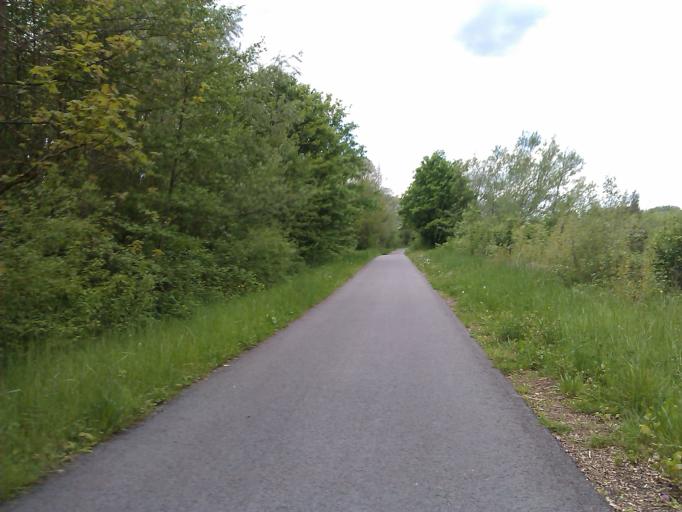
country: FR
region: Franche-Comte
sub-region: Departement du Doubs
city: Sochaux
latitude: 47.5040
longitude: 6.8156
